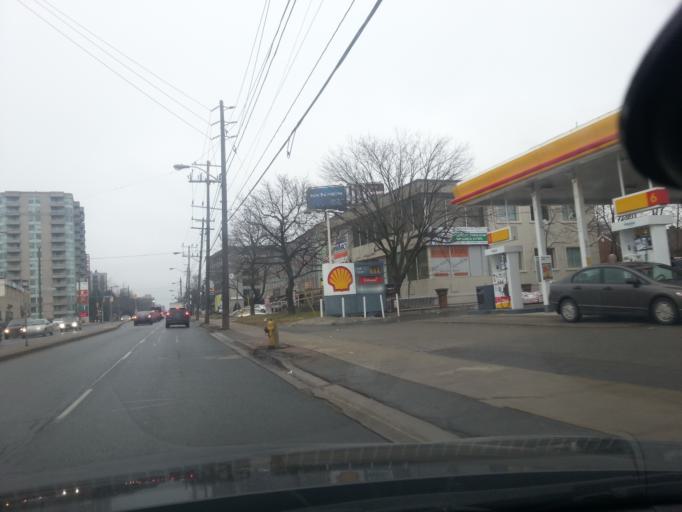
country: CA
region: Ontario
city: Toronto
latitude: 43.7195
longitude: -79.4297
